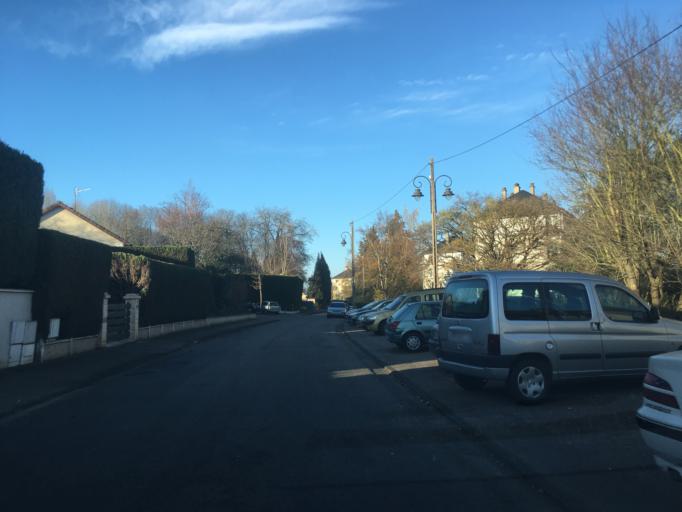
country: FR
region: Haute-Normandie
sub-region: Departement de l'Eure
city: Saint-Marcel
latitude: 49.1011
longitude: 1.4439
